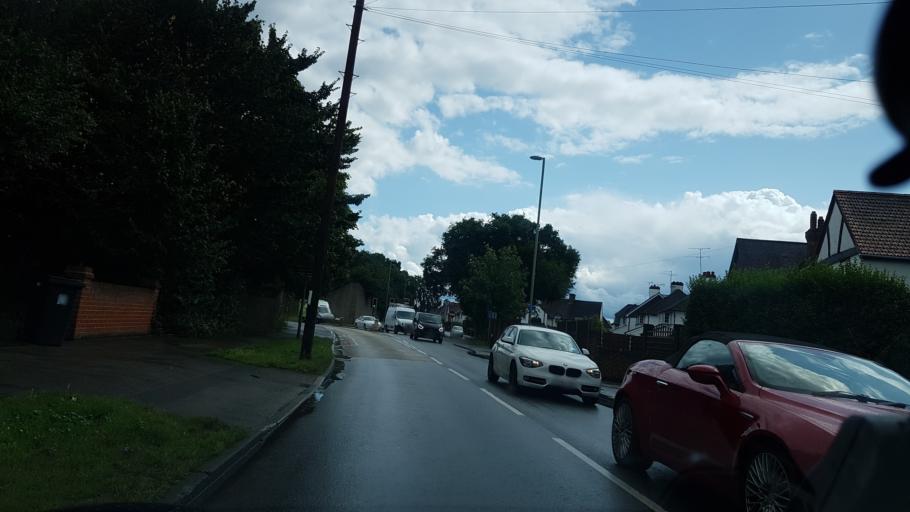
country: GB
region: England
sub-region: Surrey
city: Byfleet
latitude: 51.3451
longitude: -0.4792
